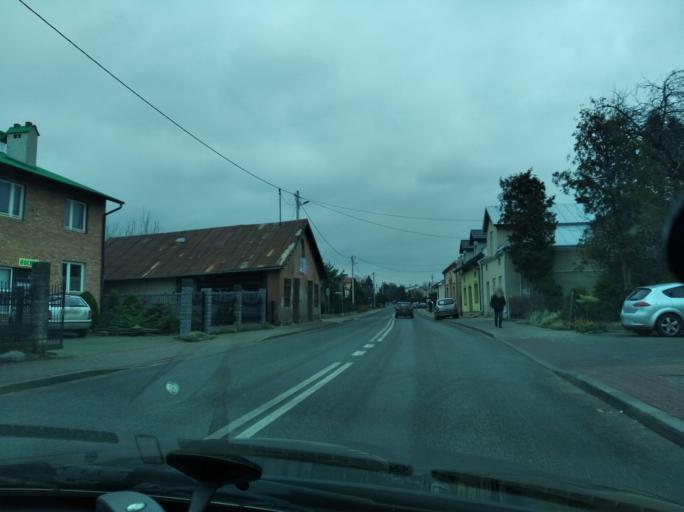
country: PL
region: Subcarpathian Voivodeship
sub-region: Powiat przeworski
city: Kanczuga
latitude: 49.9836
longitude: 22.4102
